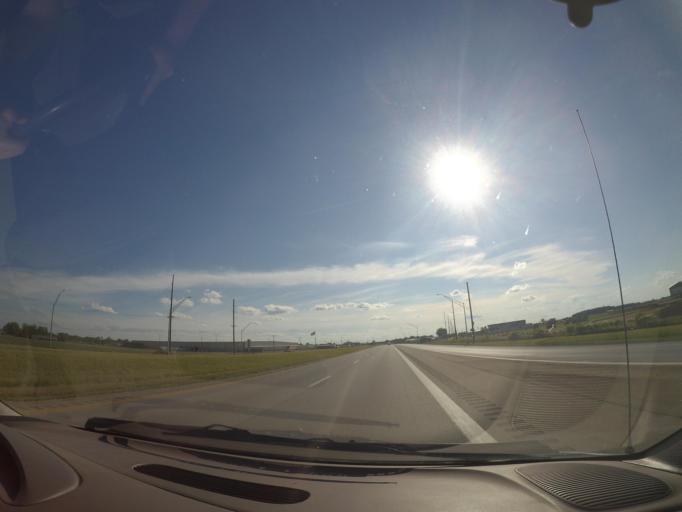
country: US
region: Ohio
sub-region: Henry County
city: Napoleon
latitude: 41.4136
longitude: -84.1089
